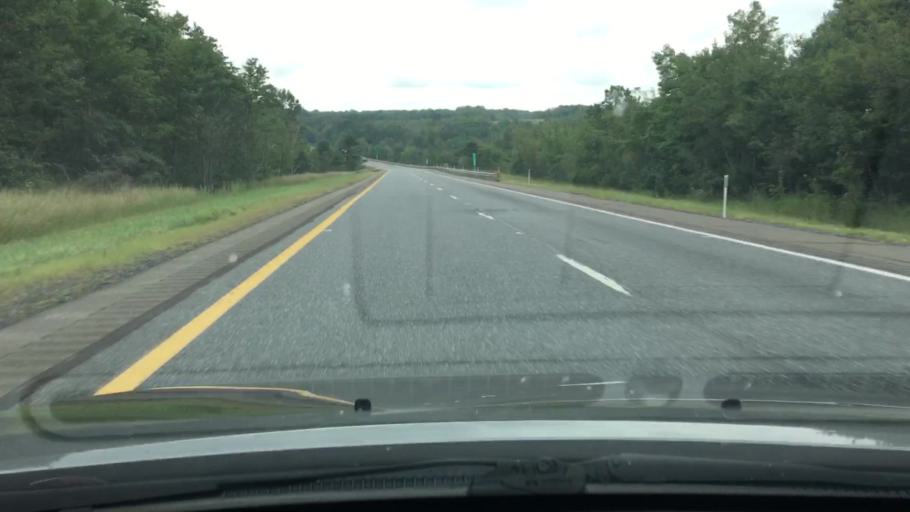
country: US
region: Pennsylvania
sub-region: Schuylkill County
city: Tremont
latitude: 40.6981
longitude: -76.3688
